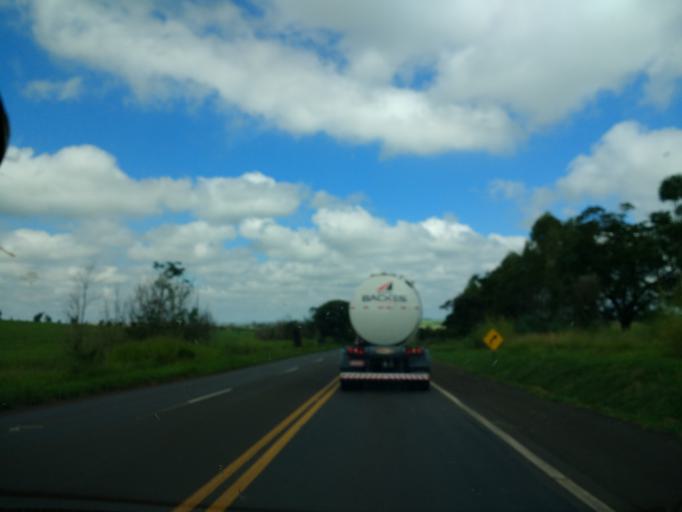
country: BR
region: Parana
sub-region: Cruzeiro Do Oeste
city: Cruzeiro do Oeste
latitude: -23.7840
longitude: -53.0260
